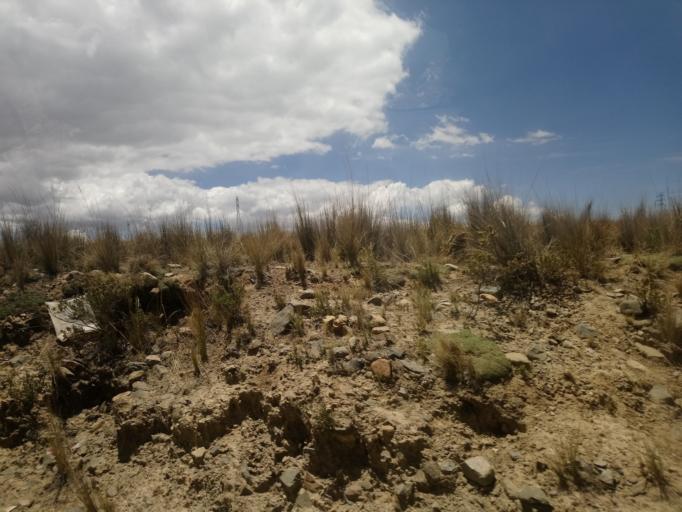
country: BO
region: La Paz
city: La Paz
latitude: -16.4363
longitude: -68.1625
